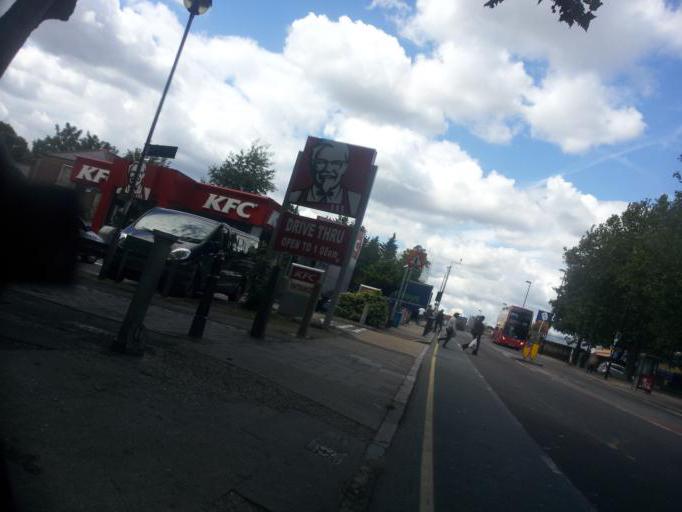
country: GB
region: England
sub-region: Greater London
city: Poplar
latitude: 51.4854
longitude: -0.0343
